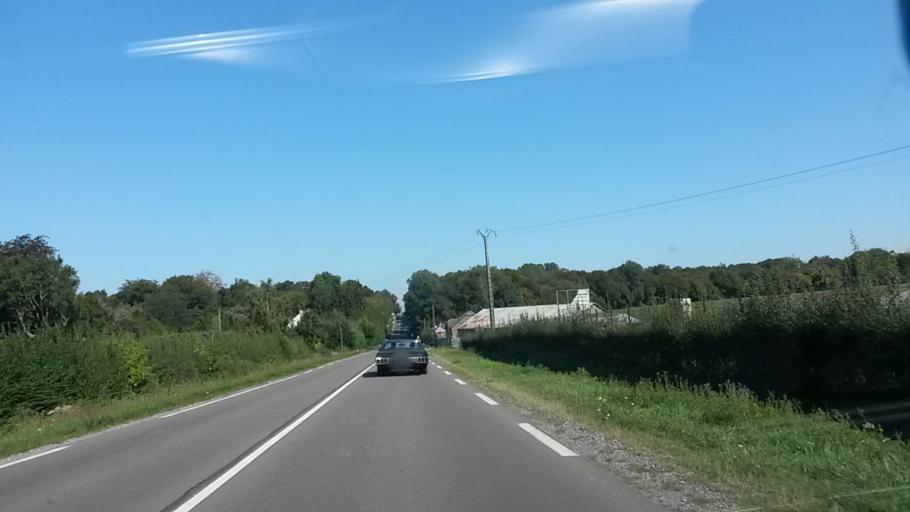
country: FR
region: Nord-Pas-de-Calais
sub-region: Departement du Nord
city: Hautmont
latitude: 50.1903
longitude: 3.9515
